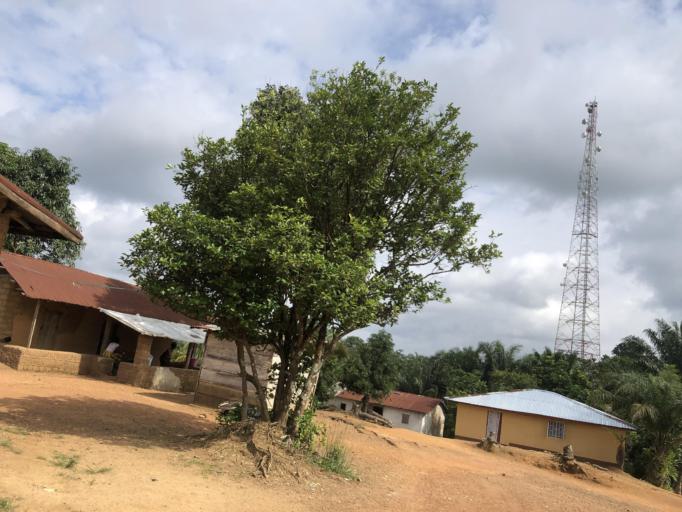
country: SL
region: Eastern Province
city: Kailahun
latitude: 8.2832
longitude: -10.5653
